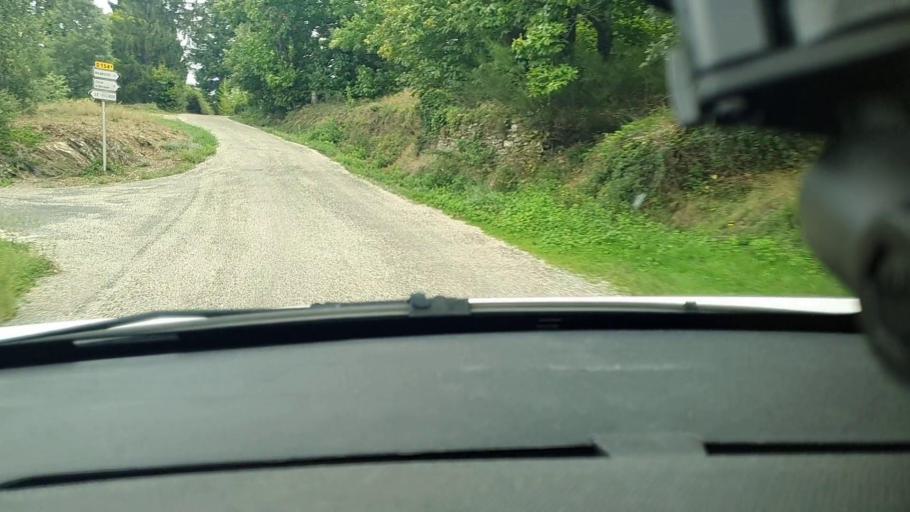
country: FR
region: Languedoc-Roussillon
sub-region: Departement du Gard
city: Branoux-les-Taillades
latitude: 44.2288
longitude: 3.9616
